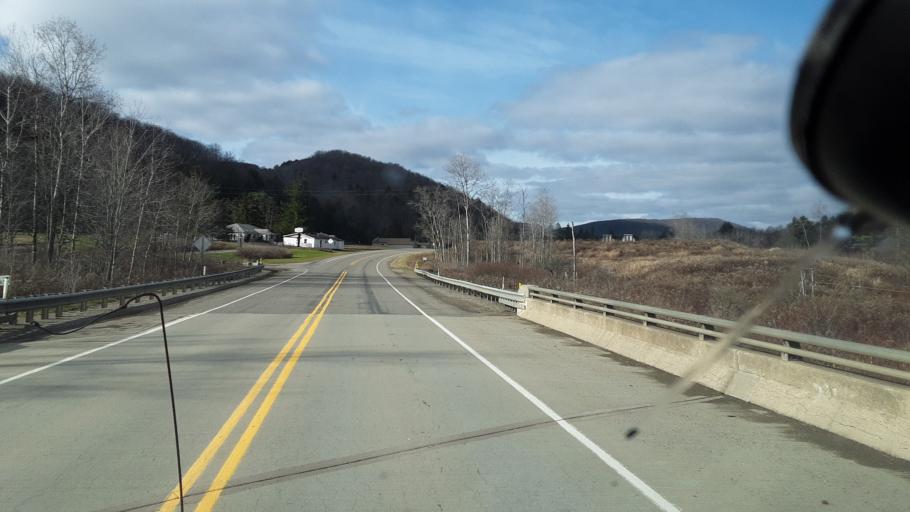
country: US
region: Pennsylvania
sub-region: Potter County
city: Galeton
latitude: 41.7817
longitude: -77.7371
